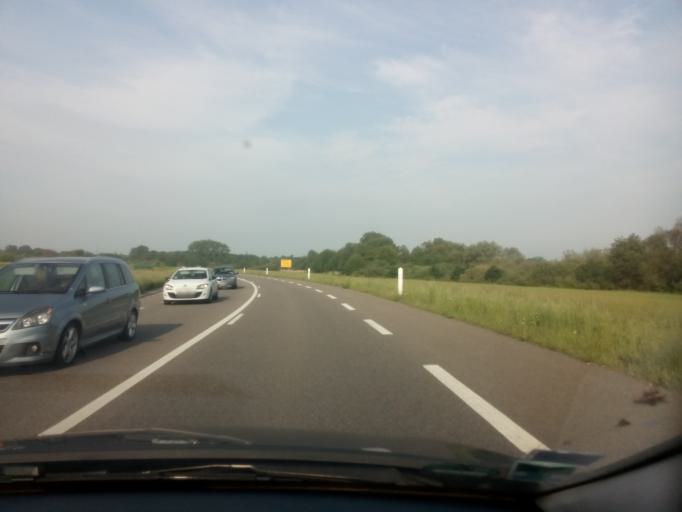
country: FR
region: Alsace
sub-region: Departement du Bas-Rhin
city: Soufflenheim
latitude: 48.8182
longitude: 7.9713
